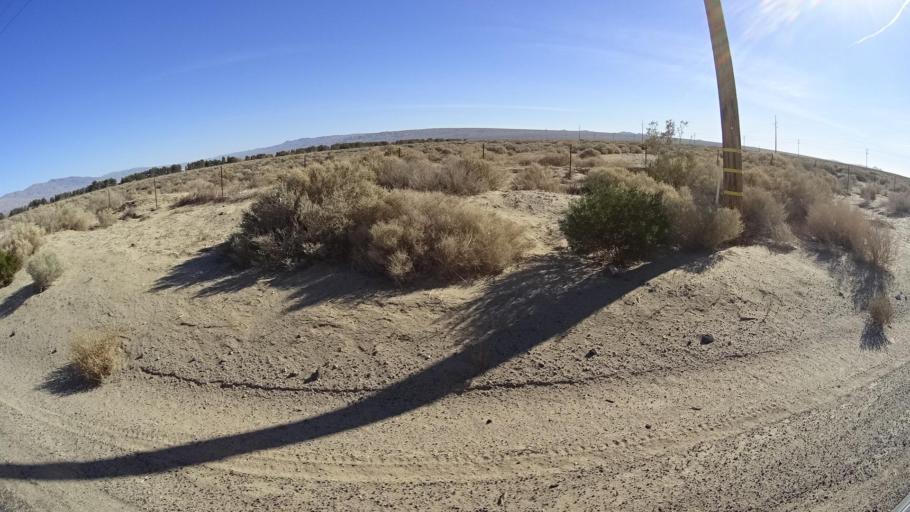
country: US
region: California
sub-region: Kern County
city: California City
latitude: 35.2583
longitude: -117.9870
